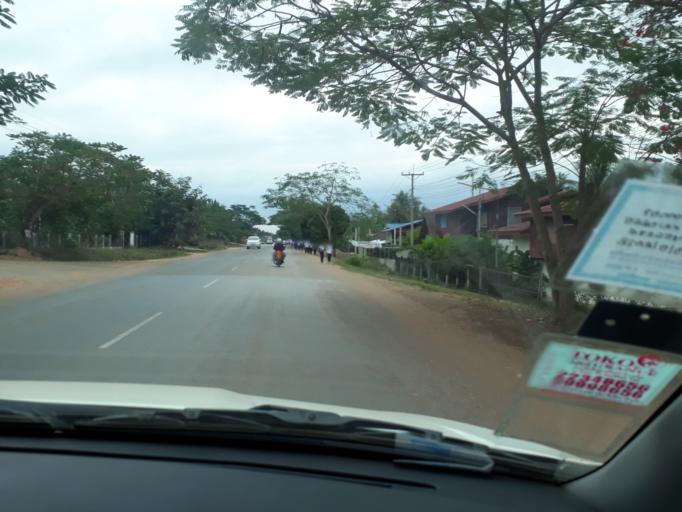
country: LA
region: Vientiane
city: Muang Phon-Hong
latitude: 18.3284
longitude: 102.4448
